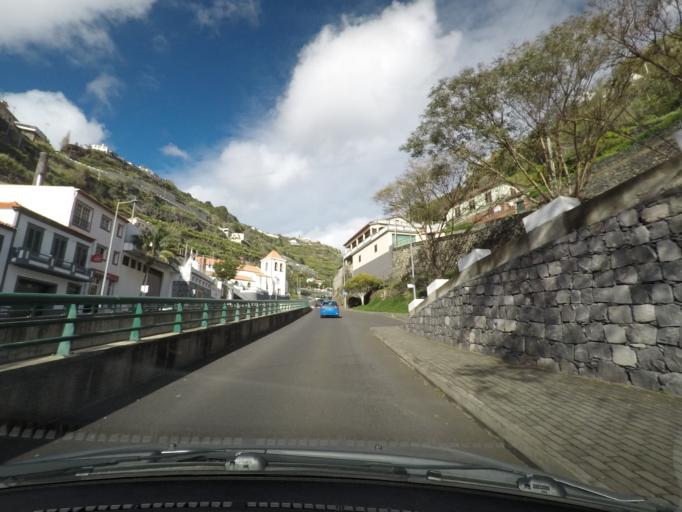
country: PT
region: Madeira
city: Calheta
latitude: 32.7222
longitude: -17.1774
